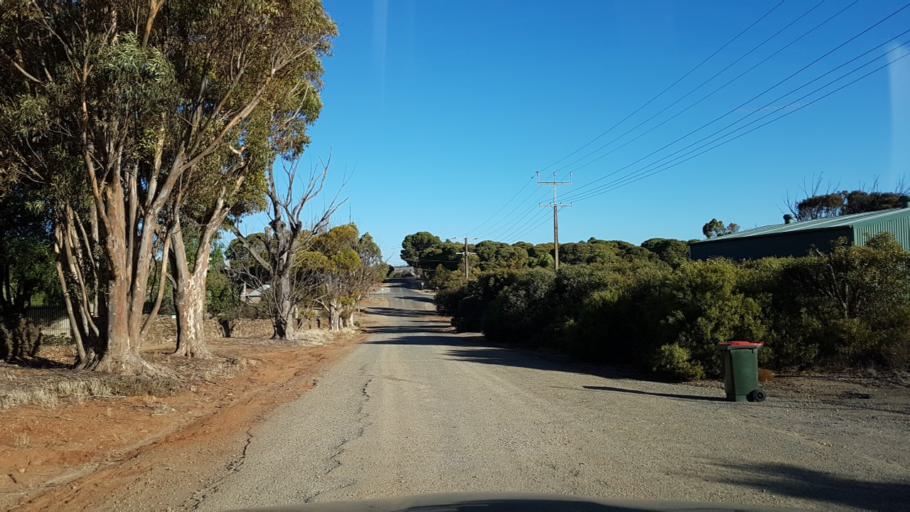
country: AU
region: South Australia
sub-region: Clare and Gilbert Valleys
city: Clare
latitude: -33.6684
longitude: 138.9335
